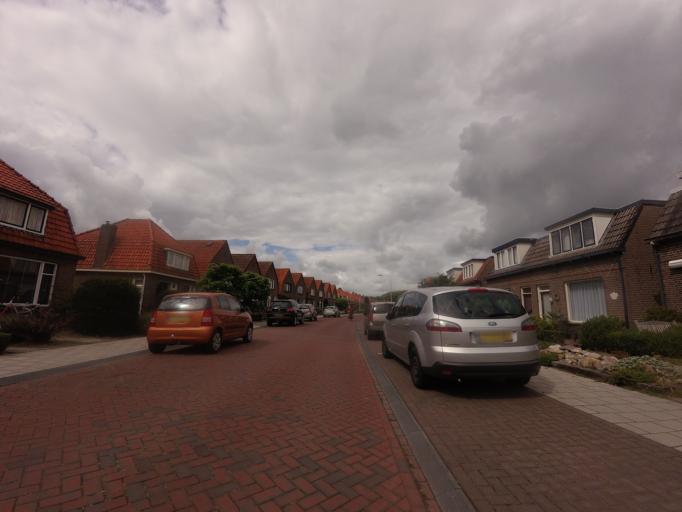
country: NL
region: Drenthe
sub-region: Gemeente Meppel
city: Meppel
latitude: 52.7077
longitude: 6.1796
